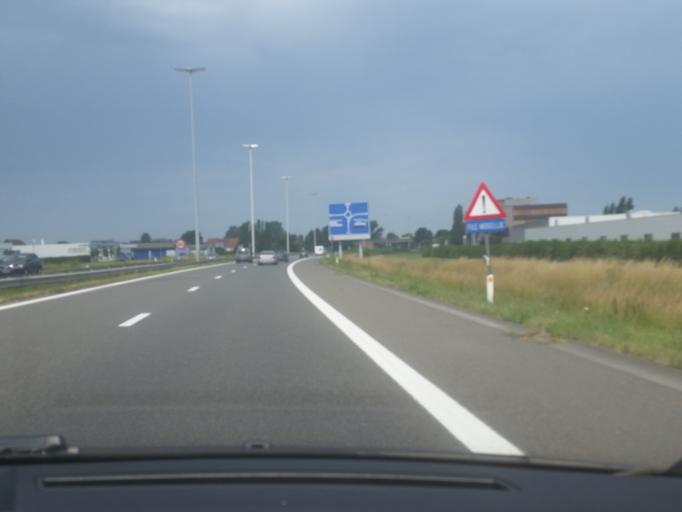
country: BE
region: Flanders
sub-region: Provincie West-Vlaanderen
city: Ostend
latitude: 51.2097
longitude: 2.9407
